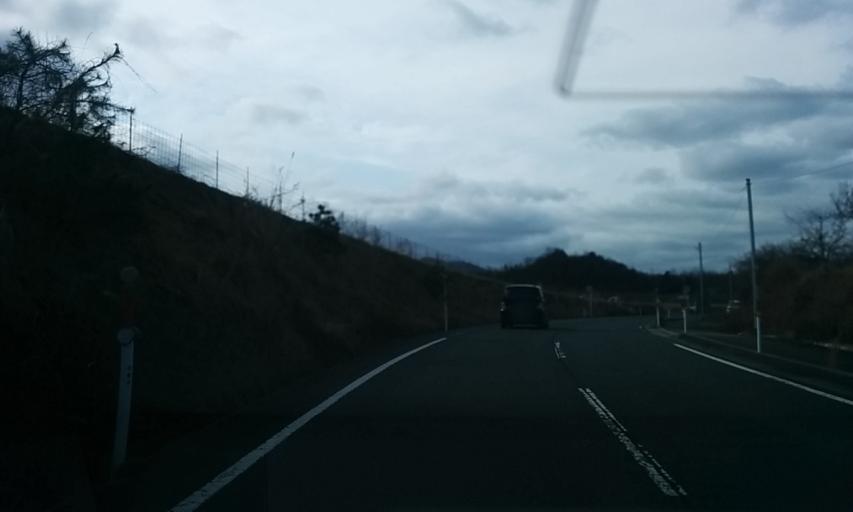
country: JP
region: Kyoto
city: Miyazu
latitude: 35.5826
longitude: 135.1053
